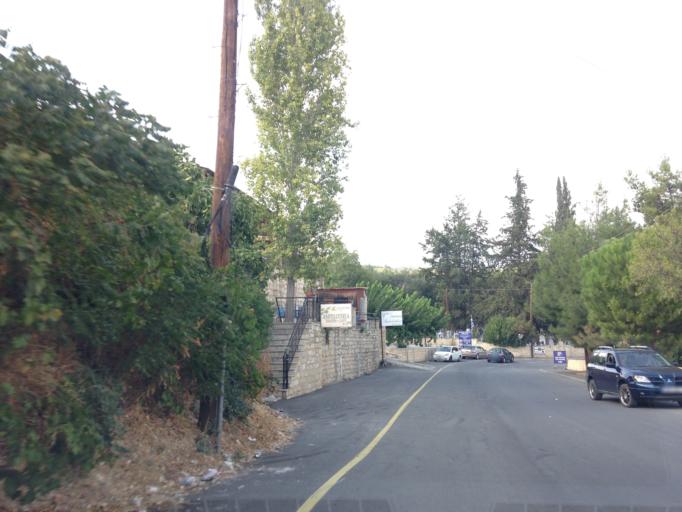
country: CY
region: Limassol
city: Pachna
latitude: 34.8472
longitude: 32.8062
